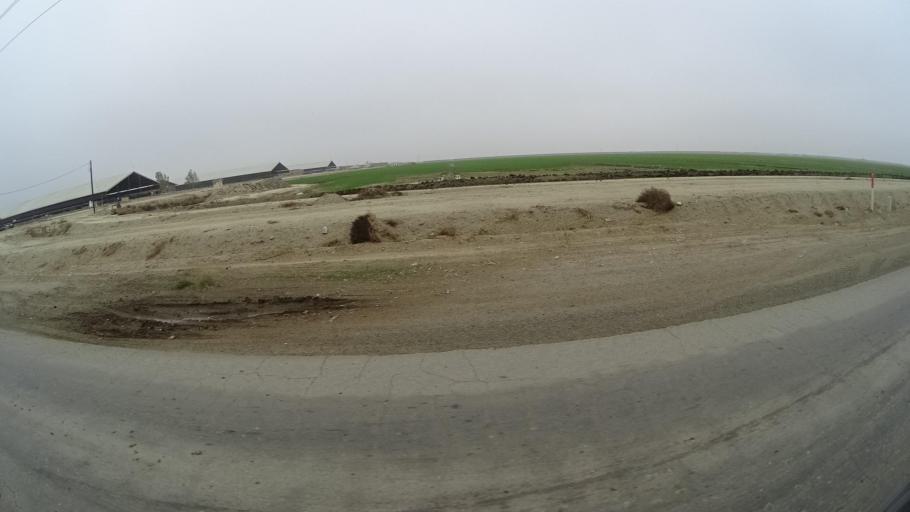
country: US
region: California
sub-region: Kern County
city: Rosedale
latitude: 35.2088
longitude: -119.1807
